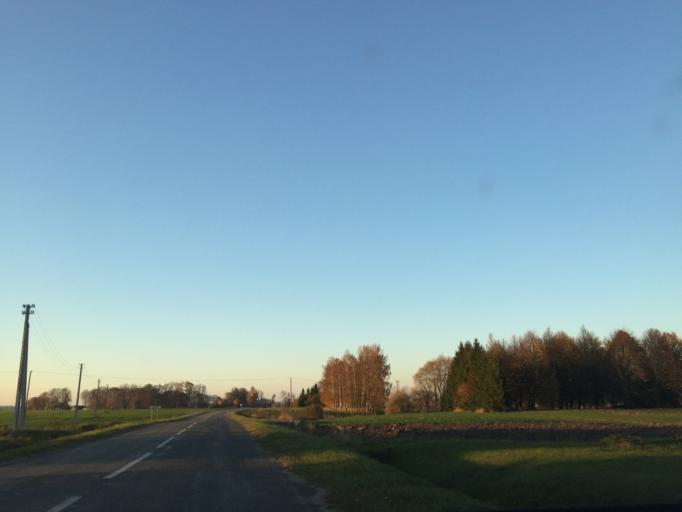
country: LT
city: Vieksniai
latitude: 56.3818
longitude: 22.5562
